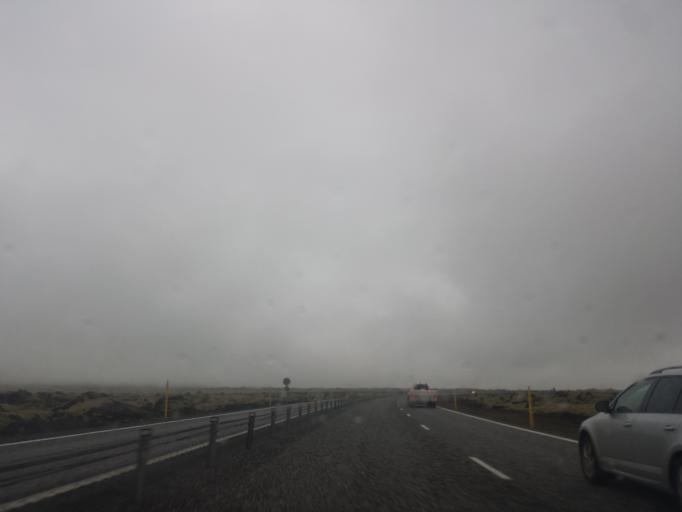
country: IS
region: South
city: THorlakshoefn
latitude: 64.0340
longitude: -21.4446
